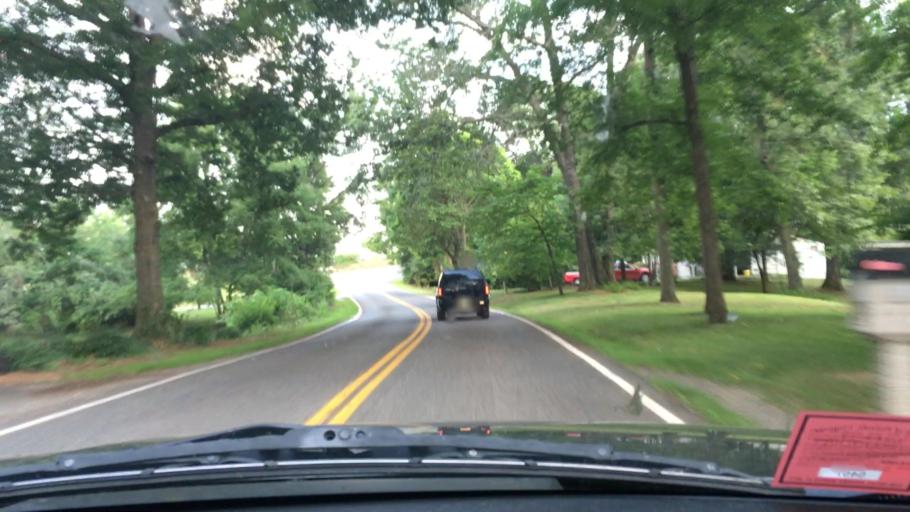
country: US
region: Virginia
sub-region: Pulaski County
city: Dublin
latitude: 37.0548
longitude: -80.6968
